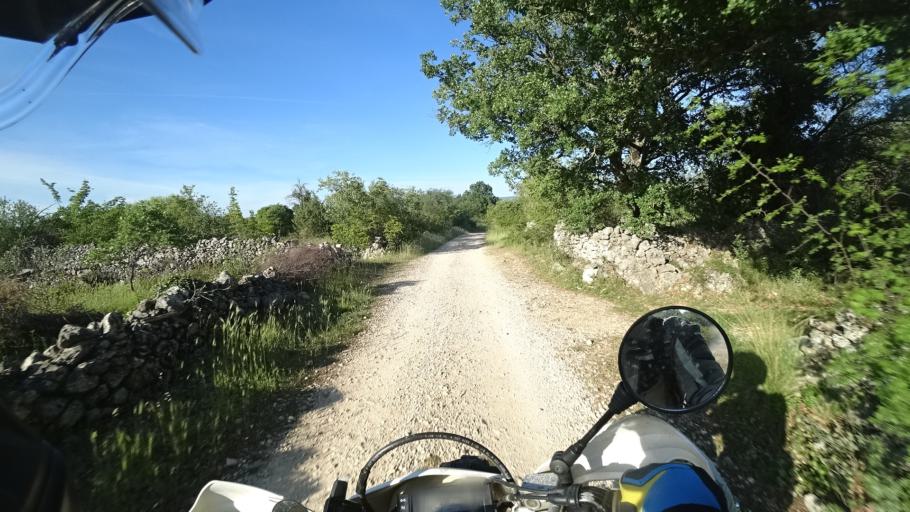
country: HR
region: Sibensko-Kniniska
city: Drnis
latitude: 43.8415
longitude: 16.0284
